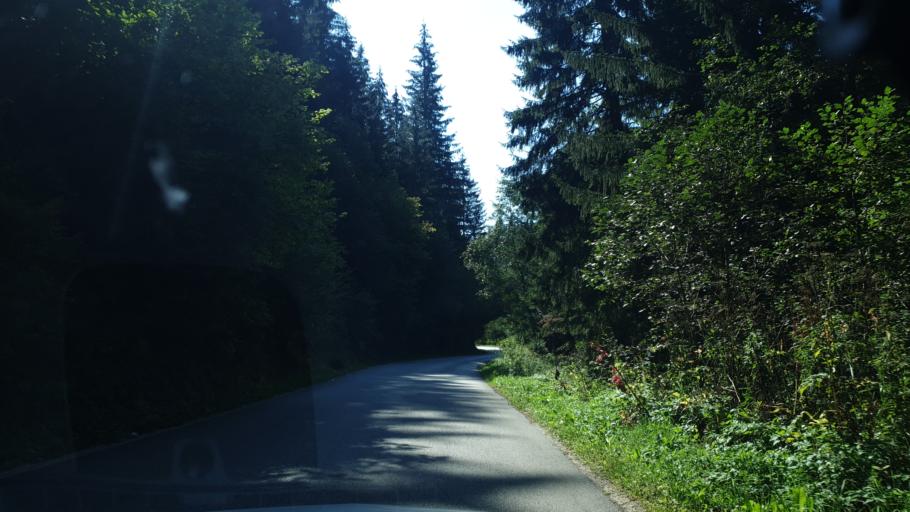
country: RS
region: Central Serbia
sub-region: Zlatiborski Okrug
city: Nova Varos
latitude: 43.4457
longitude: 19.8502
